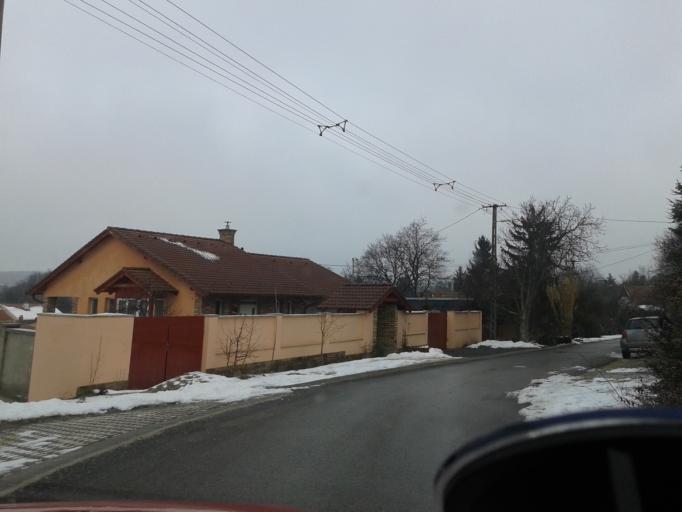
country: HU
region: Pest
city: Erd
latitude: 47.4071
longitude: 18.9272
